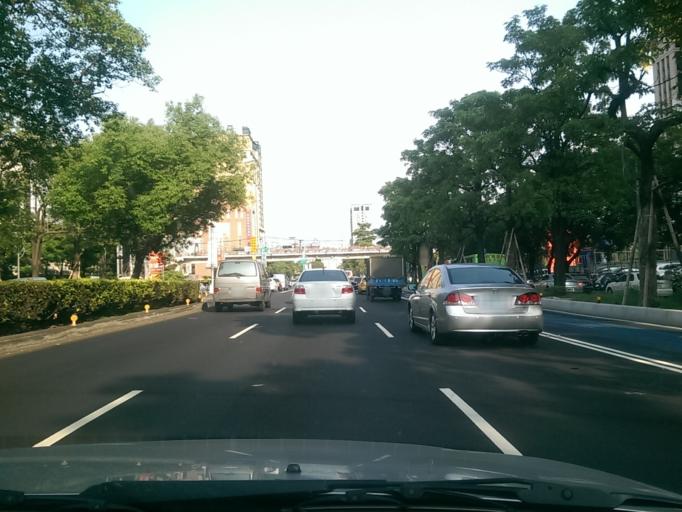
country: TW
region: Taiwan
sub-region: Taichung City
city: Taichung
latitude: 24.1649
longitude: 120.6453
